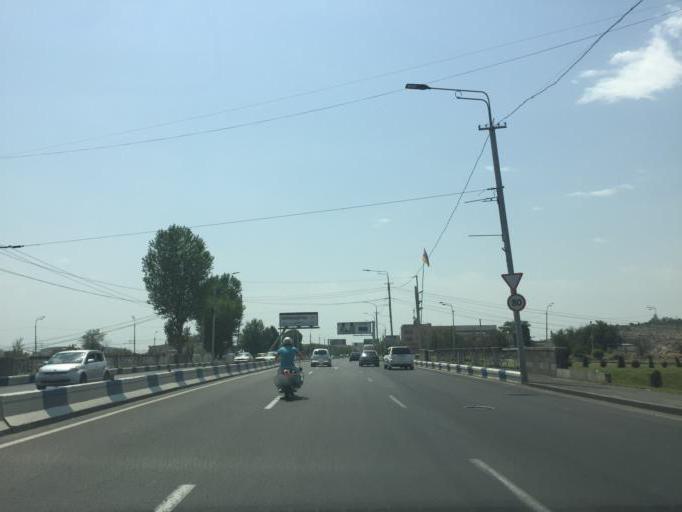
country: AM
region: Ararat
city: Argavand
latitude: 40.1601
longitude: 44.4685
